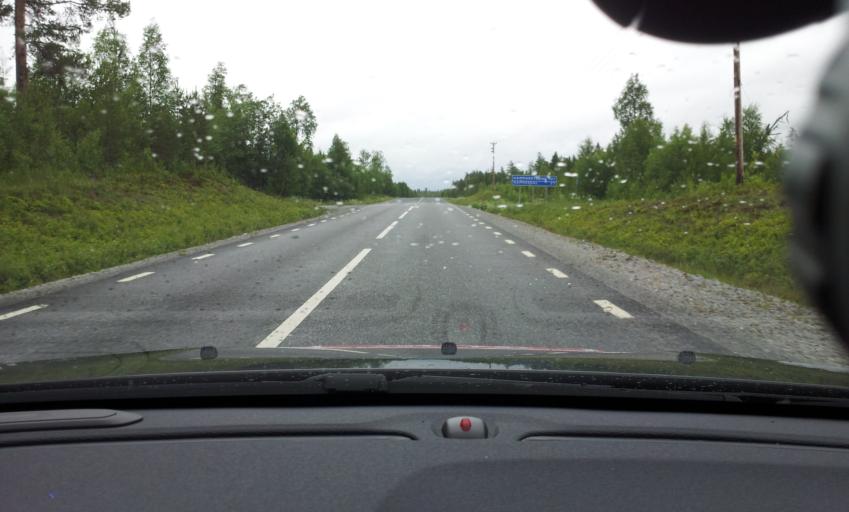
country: SE
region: Jaemtland
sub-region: OEstersunds Kommun
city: Lit
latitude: 63.7365
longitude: 14.7471
